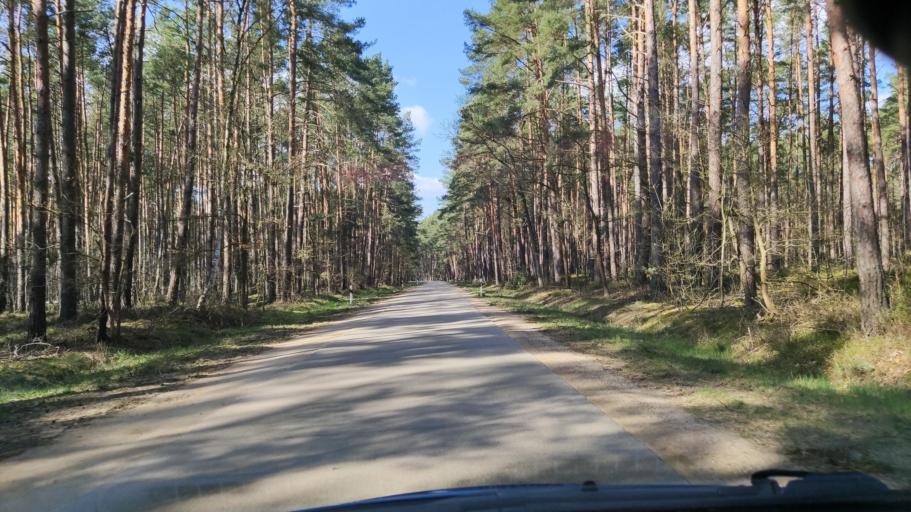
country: DE
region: Lower Saxony
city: Trebel
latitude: 52.9985
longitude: 11.2914
